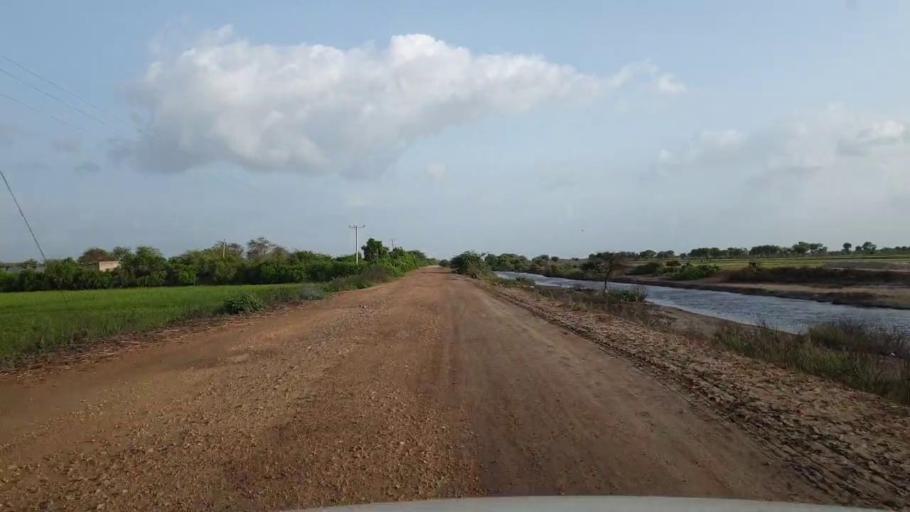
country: PK
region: Sindh
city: Kario
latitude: 24.8130
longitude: 68.6468
